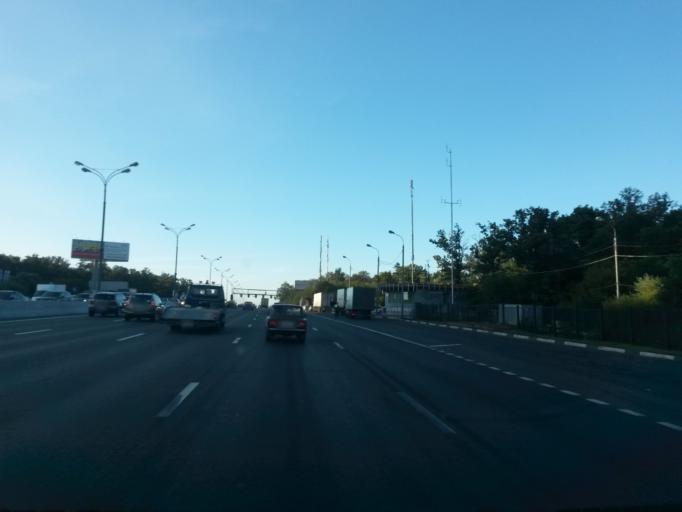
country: RU
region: Moscow
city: Vostochnyy
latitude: 55.8054
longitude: 37.8393
